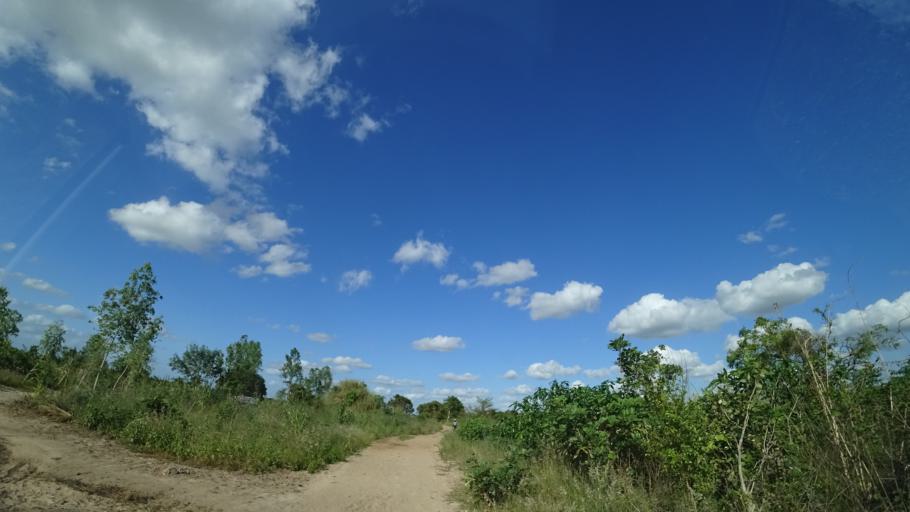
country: MZ
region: Sofala
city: Dondo
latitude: -19.4309
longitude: 34.7289
